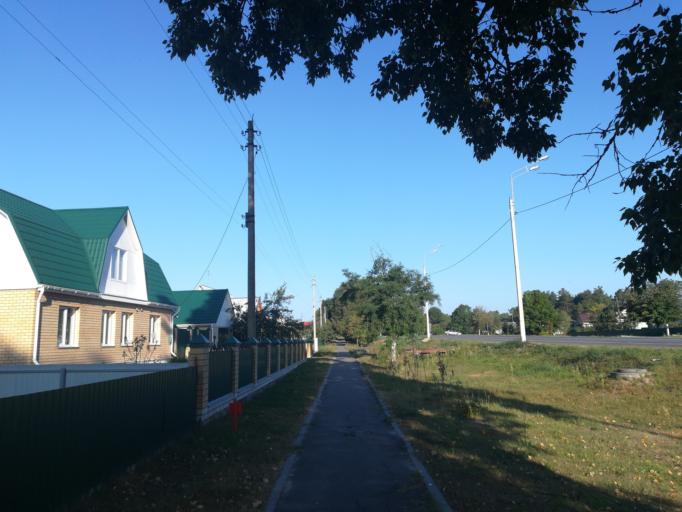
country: RU
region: Brjansk
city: Karachev
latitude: 53.1278
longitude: 34.9385
